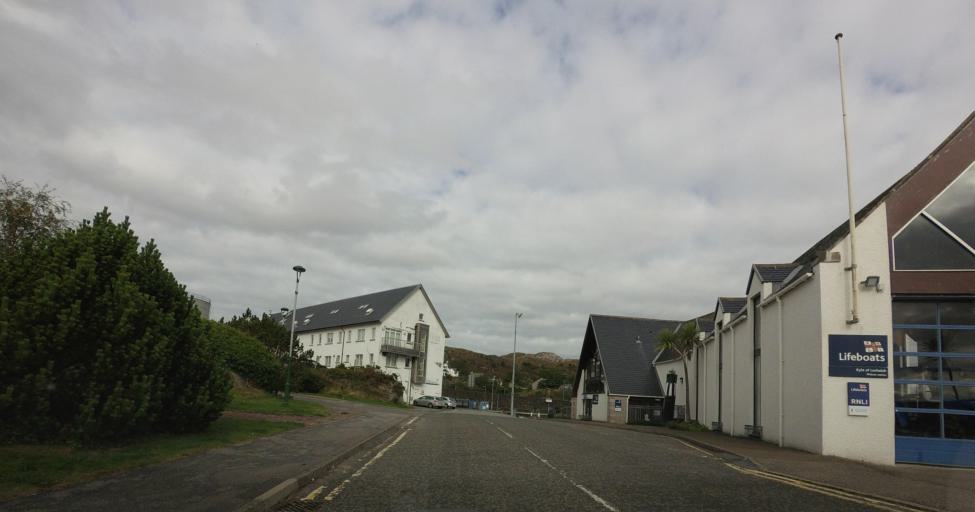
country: GB
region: Scotland
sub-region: Highland
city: Portree
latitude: 57.2801
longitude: -5.7152
